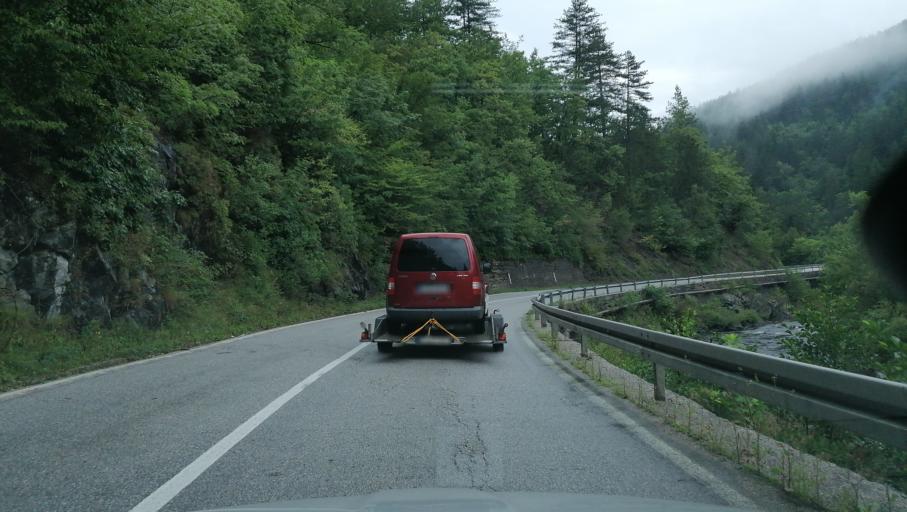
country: RS
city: Durici
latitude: 43.7784
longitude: 19.3722
